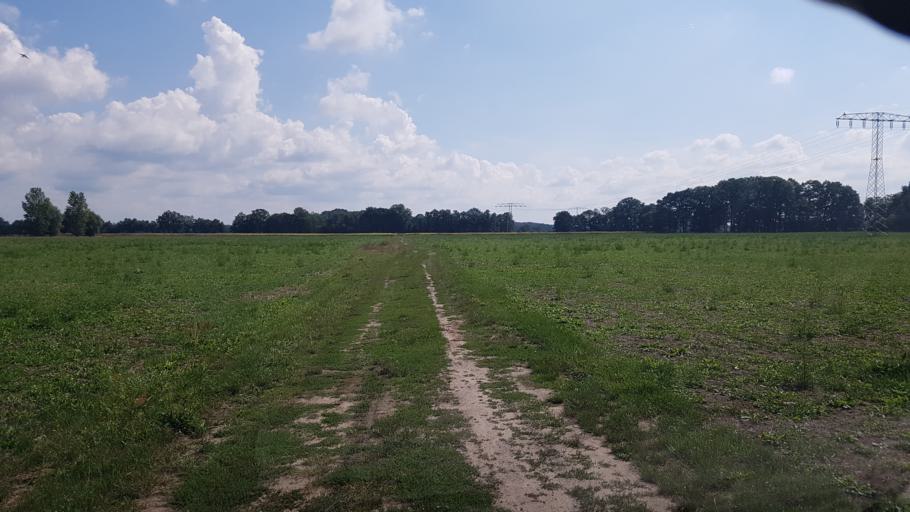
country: DE
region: Brandenburg
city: Sonnewalde
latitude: 51.6718
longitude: 13.6595
